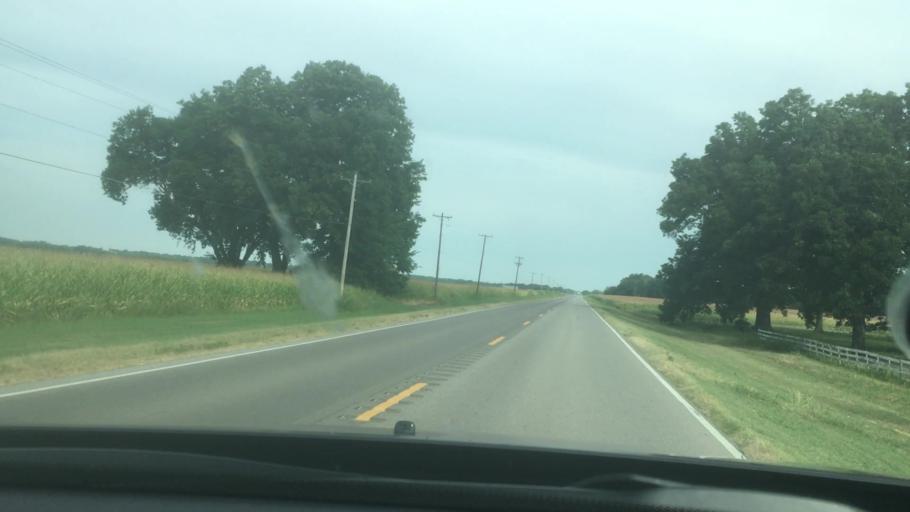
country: US
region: Oklahoma
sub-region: Garvin County
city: Pauls Valley
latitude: 34.7716
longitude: -97.3104
